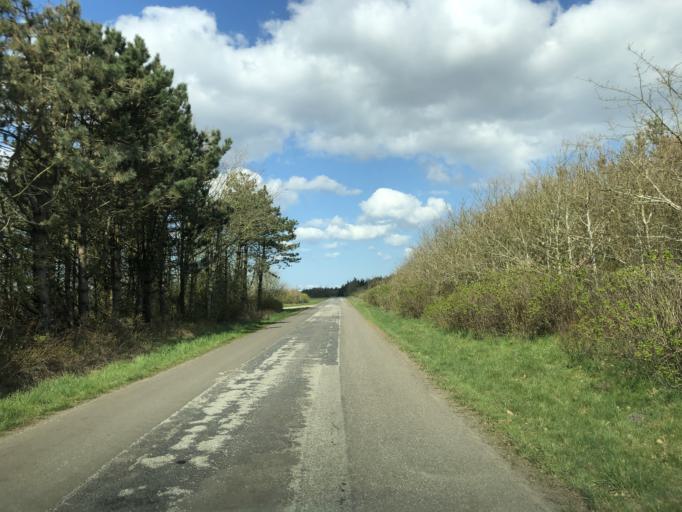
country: DK
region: Central Jutland
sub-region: Holstebro Kommune
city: Ulfborg
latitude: 56.3710
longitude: 8.2189
